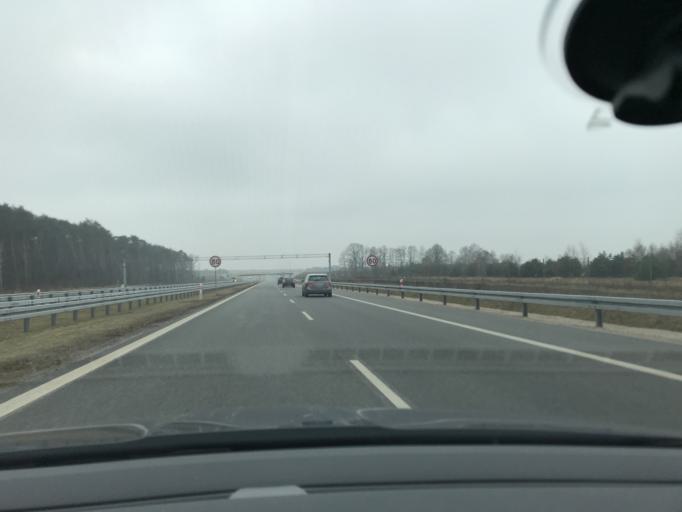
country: PL
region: Lodz Voivodeship
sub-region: Powiat pabianicki
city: Dobron
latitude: 51.6111
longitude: 19.2746
